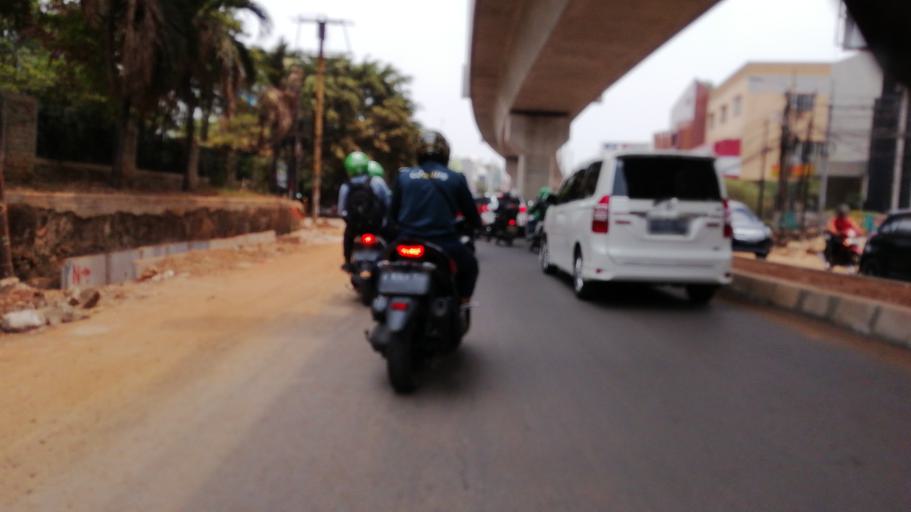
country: ID
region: Banten
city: South Tangerang
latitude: -6.2828
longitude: 106.7960
